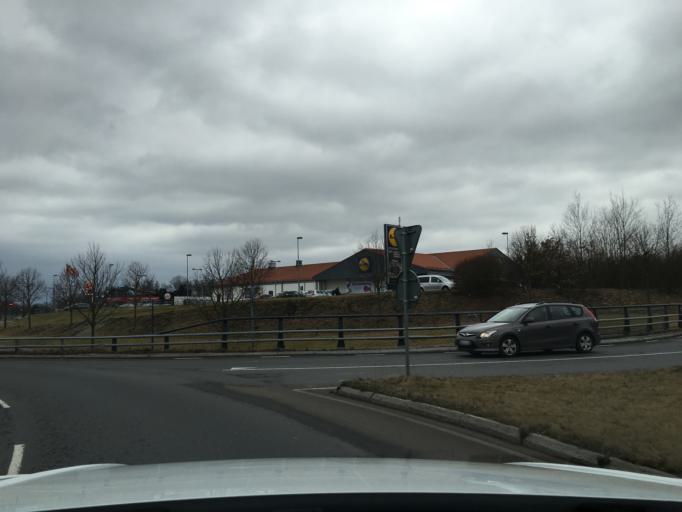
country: SE
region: Halland
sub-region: Halmstads Kommun
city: Halmstad
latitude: 56.6674
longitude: 12.8225
